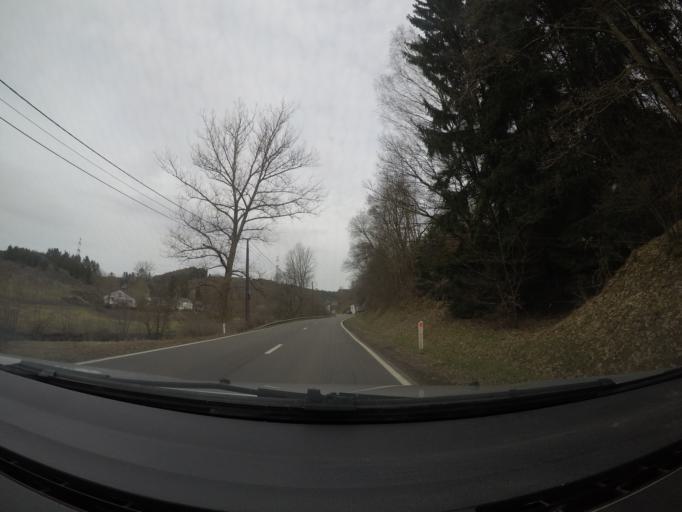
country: BE
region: Wallonia
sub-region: Province du Luxembourg
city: Martelange
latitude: 49.8440
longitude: 5.7172
